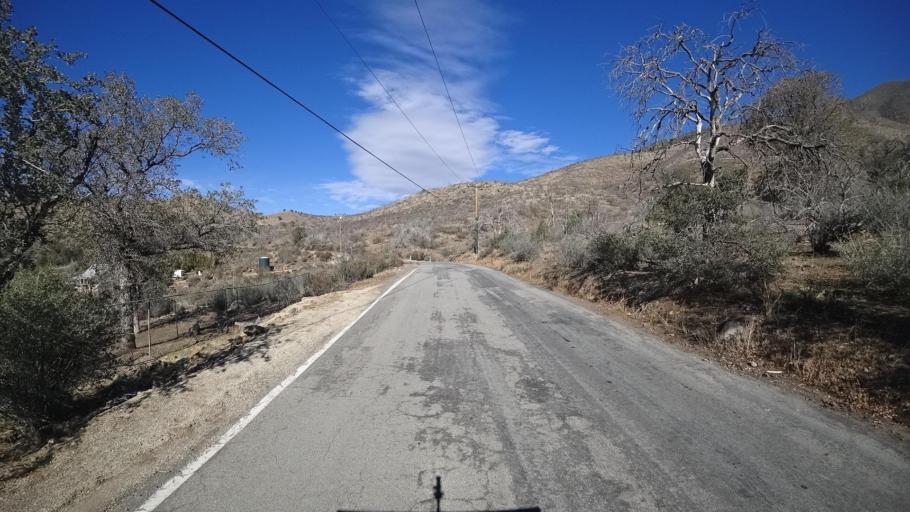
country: US
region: California
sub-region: Kern County
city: Bodfish
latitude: 35.5505
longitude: -118.5056
